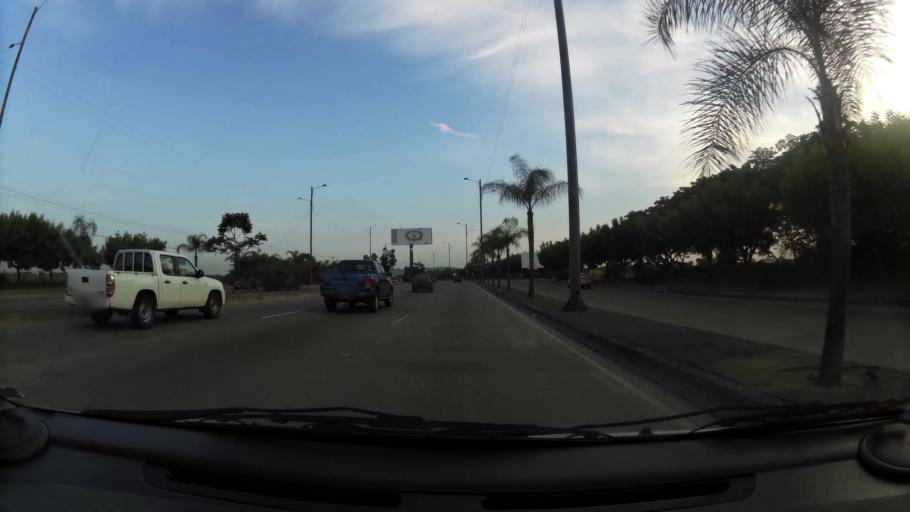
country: EC
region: Guayas
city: Eloy Alfaro
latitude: -2.1018
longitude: -79.8890
